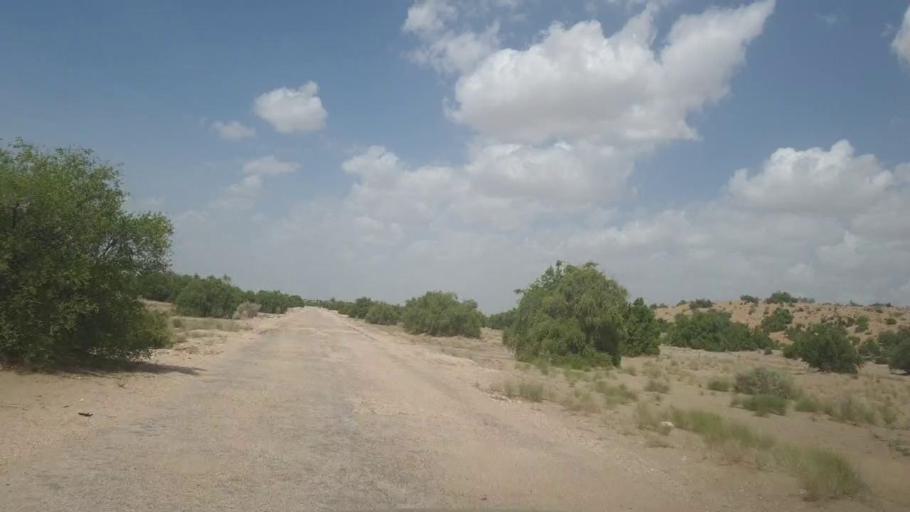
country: PK
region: Sindh
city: Kot Diji
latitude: 27.2583
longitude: 69.1700
